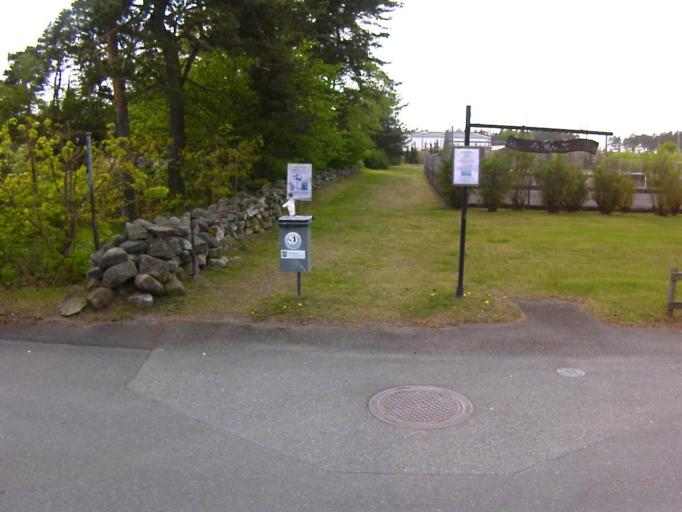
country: SE
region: Skane
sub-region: Kristianstads Kommun
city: Fjalkinge
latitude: 56.0457
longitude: 14.2637
